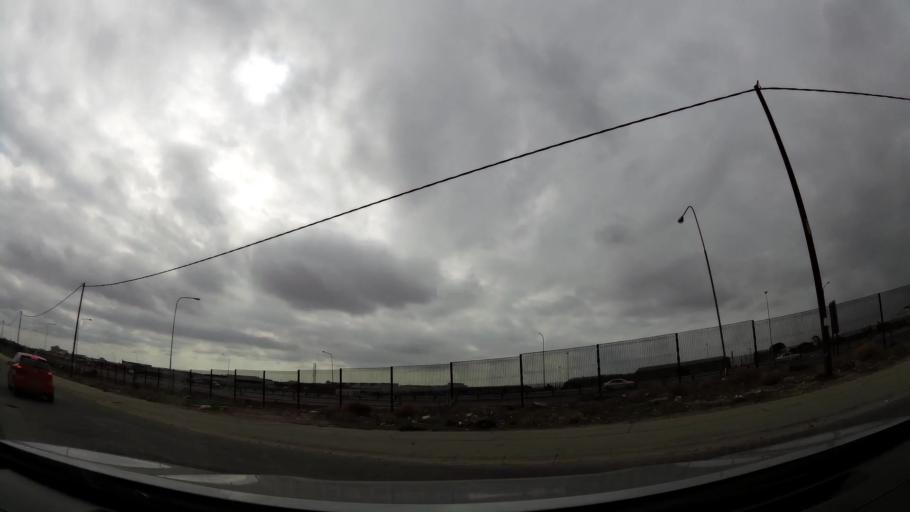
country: ZA
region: Eastern Cape
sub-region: Nelson Mandela Bay Metropolitan Municipality
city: Port Elizabeth
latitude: -33.8913
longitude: 25.5634
